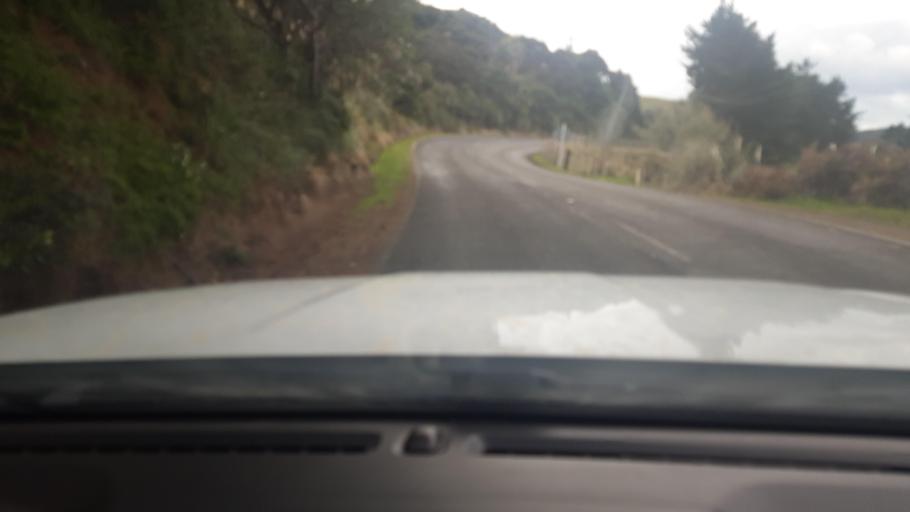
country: NZ
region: Northland
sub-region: Far North District
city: Ahipara
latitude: -35.2726
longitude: 173.2094
